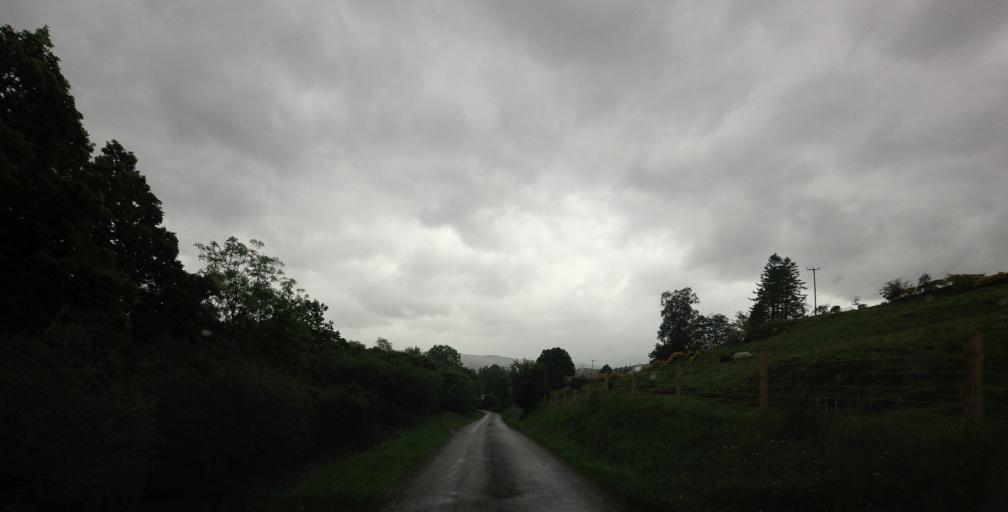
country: GB
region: Scotland
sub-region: Argyll and Bute
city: Oban
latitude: 56.7126
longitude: -5.5629
